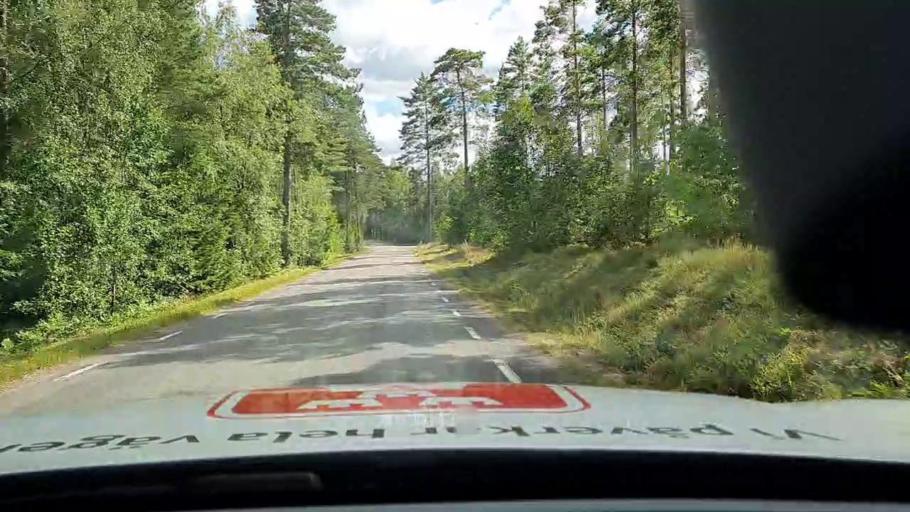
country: SE
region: Vaestra Goetaland
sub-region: Karlsborgs Kommun
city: Molltorp
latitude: 58.6053
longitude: 14.3677
